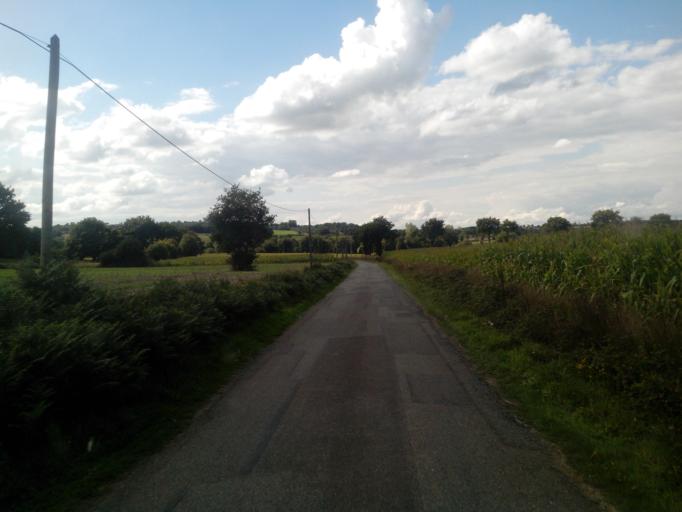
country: FR
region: Brittany
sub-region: Departement d'Ille-et-Vilaine
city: Boisgervilly
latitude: 48.0973
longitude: -2.1201
